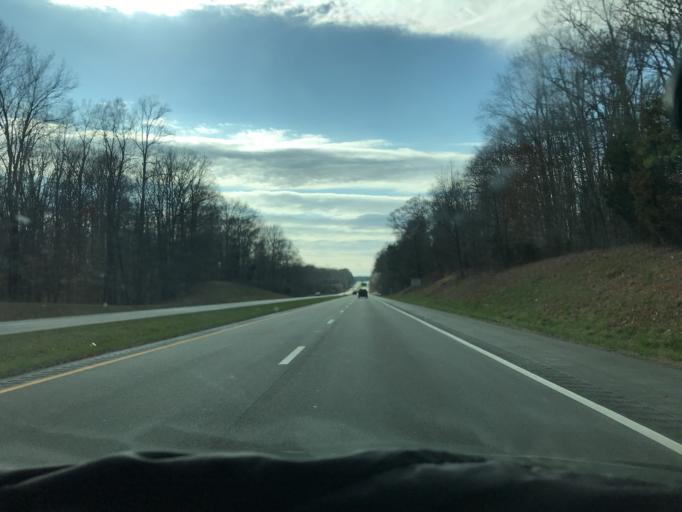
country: US
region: Virginia
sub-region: Chesterfield County
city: Brandermill
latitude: 37.4634
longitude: -77.6153
